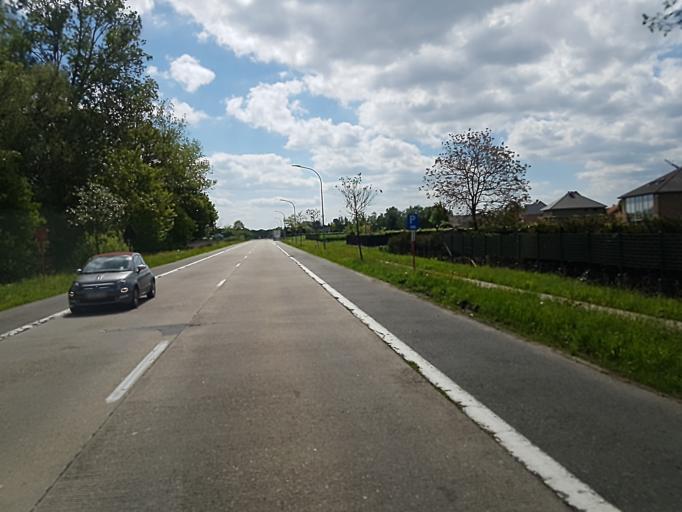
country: BE
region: Flanders
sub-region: Provincie Antwerpen
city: Westerlo
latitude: 51.0868
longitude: 4.9495
